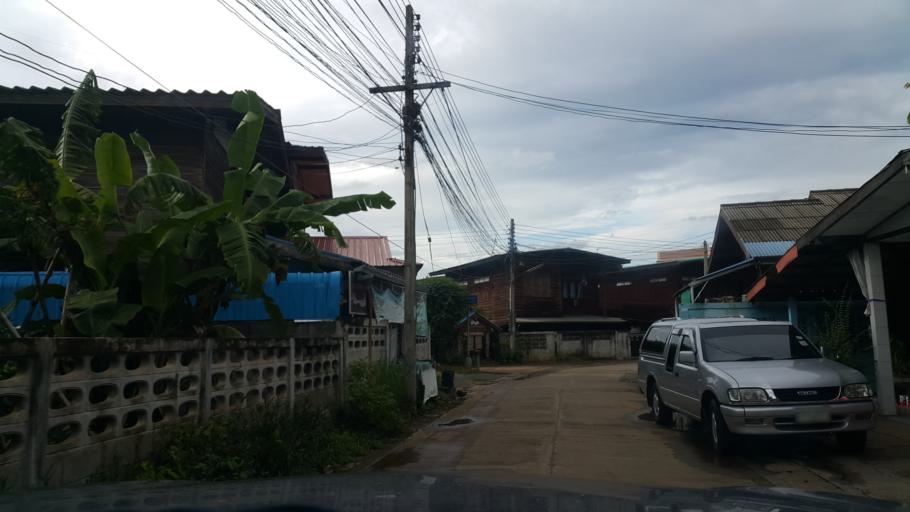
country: TH
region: Sukhothai
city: Thung Saliam
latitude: 17.3168
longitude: 99.5494
